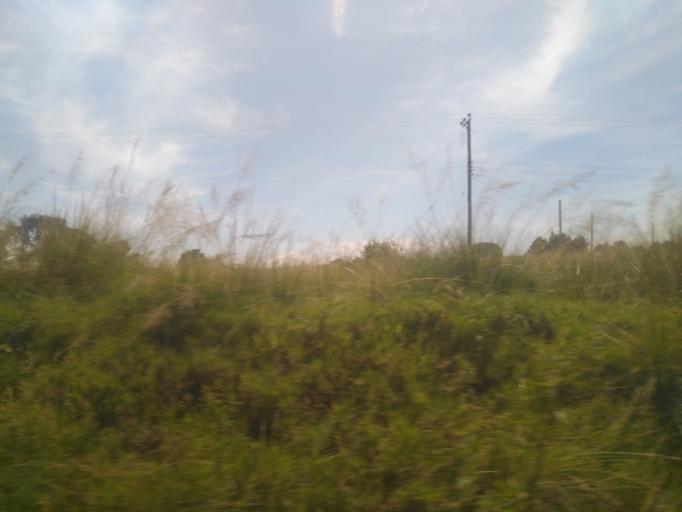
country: UG
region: Central Region
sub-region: Wakiso District
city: Entebbe
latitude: 0.0370
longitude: 32.4303
